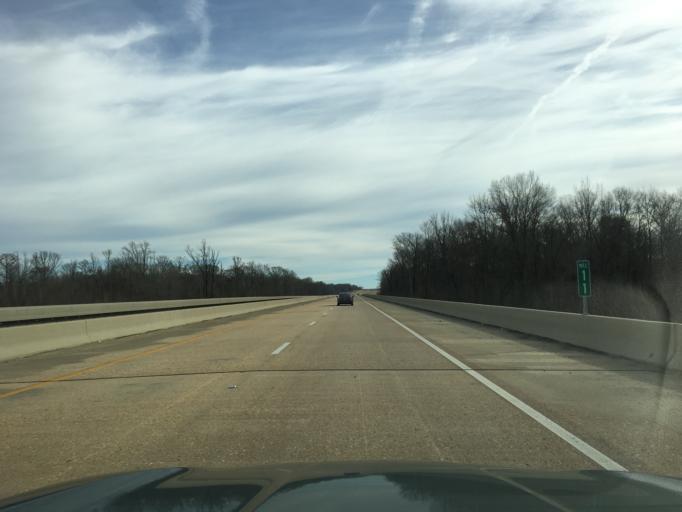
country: US
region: Mississippi
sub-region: De Soto County
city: Olive Branch
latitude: 34.8694
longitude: -89.8031
